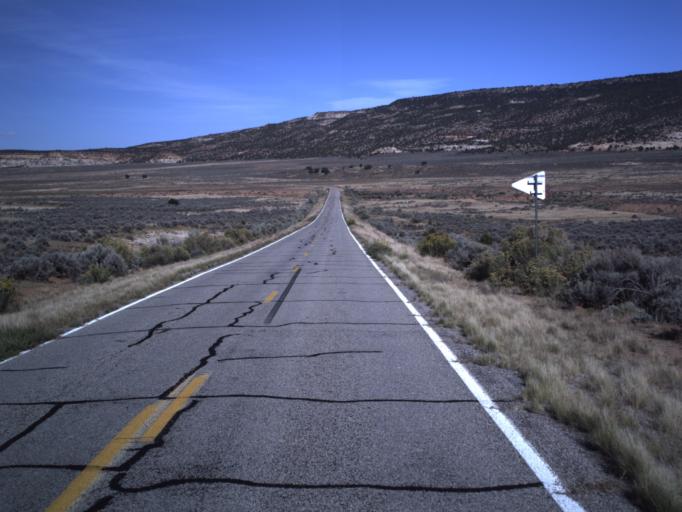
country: US
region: Utah
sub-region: San Juan County
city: Monticello
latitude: 38.0067
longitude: -109.4449
